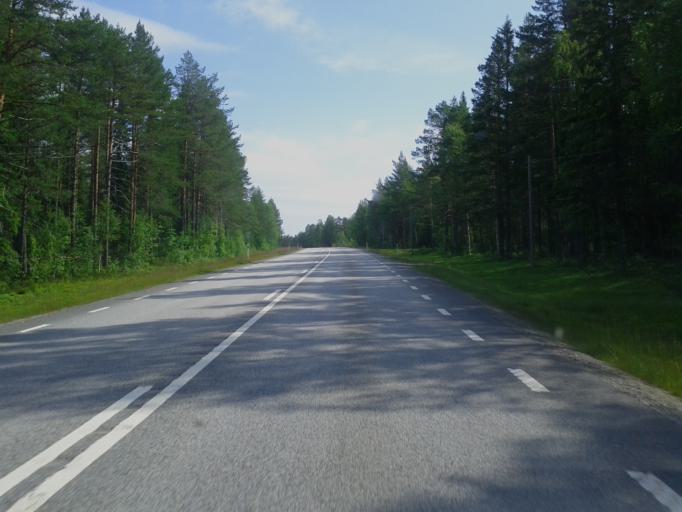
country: SE
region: Vaesterbotten
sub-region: Robertsfors Kommun
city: Robertsfors
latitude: 64.1818
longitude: 20.9809
